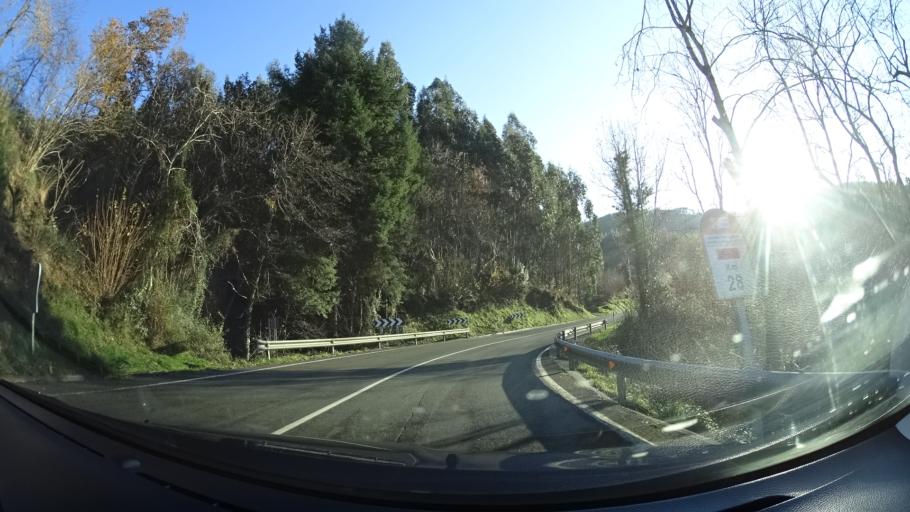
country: ES
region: Basque Country
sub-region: Bizkaia
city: Bakio
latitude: 43.3866
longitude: -2.7710
